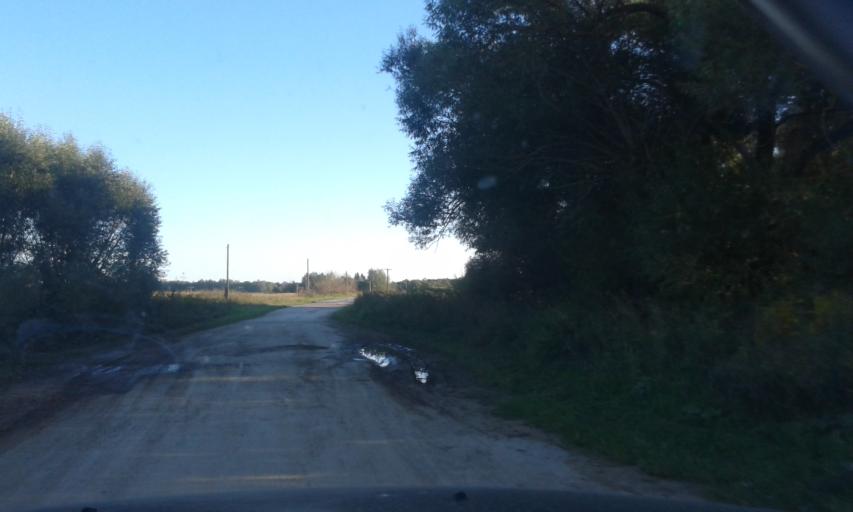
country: RU
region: Tula
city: Krapivna
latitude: 54.1211
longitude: 37.1530
